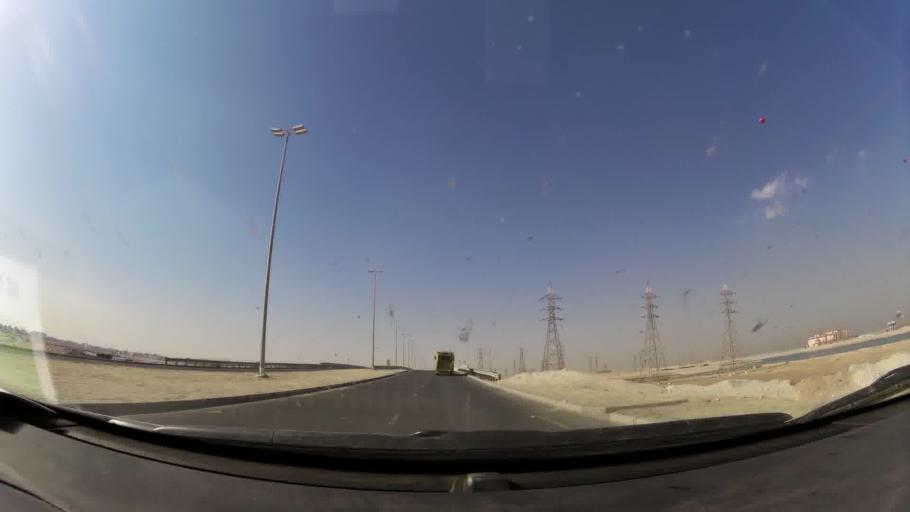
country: SA
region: Eastern Province
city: Al Khafji
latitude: 28.6751
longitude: 48.3574
